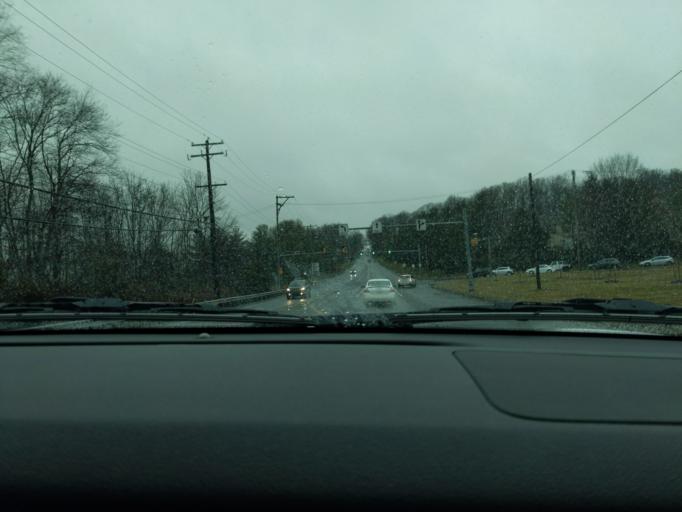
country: US
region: Pennsylvania
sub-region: Bucks County
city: Doylestown
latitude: 40.3346
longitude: -75.1400
